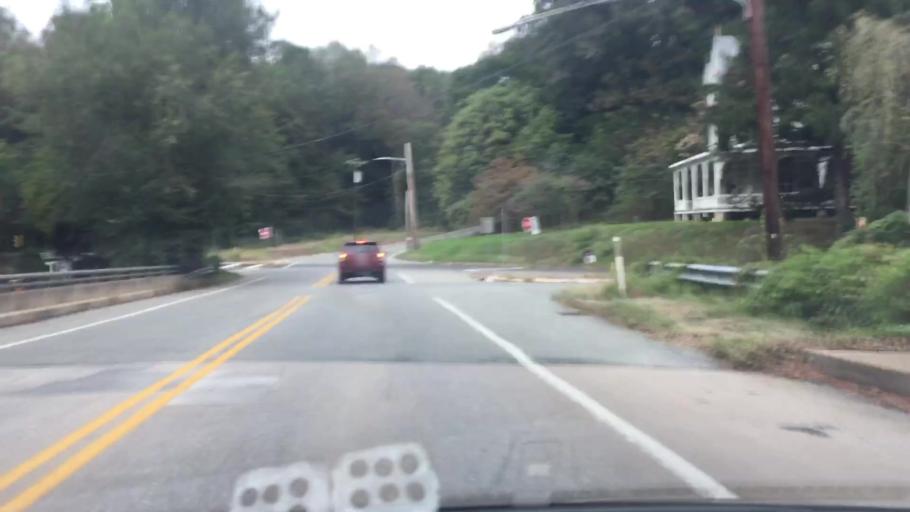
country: US
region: Pennsylvania
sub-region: Delaware County
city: Village Green-Green Ridge
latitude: 39.8694
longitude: -75.4087
